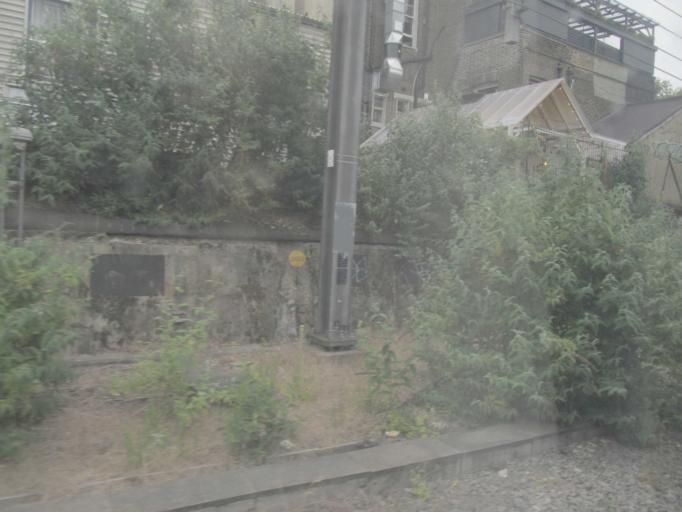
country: GB
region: England
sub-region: Greater London
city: Bayswater
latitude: 51.5232
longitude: -0.2079
